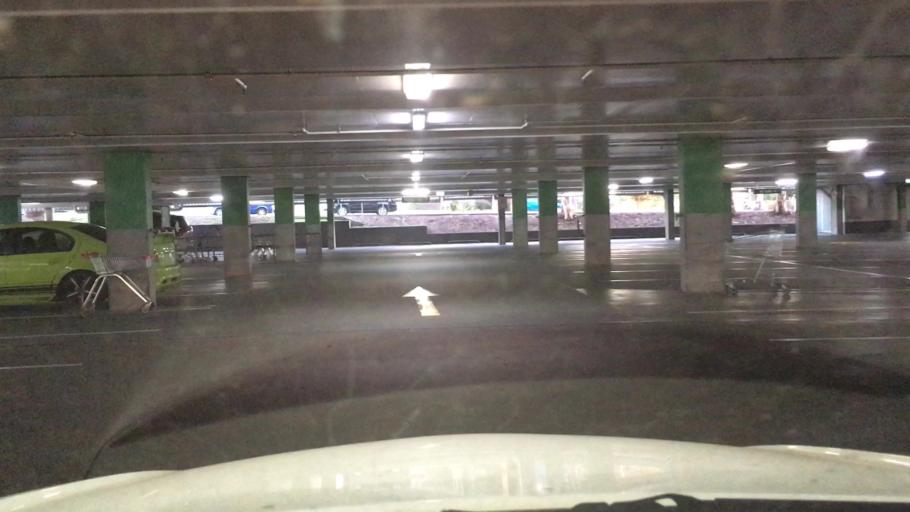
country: AU
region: Victoria
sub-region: Greater Dandenong
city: Dandenong
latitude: -37.9871
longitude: 145.2192
